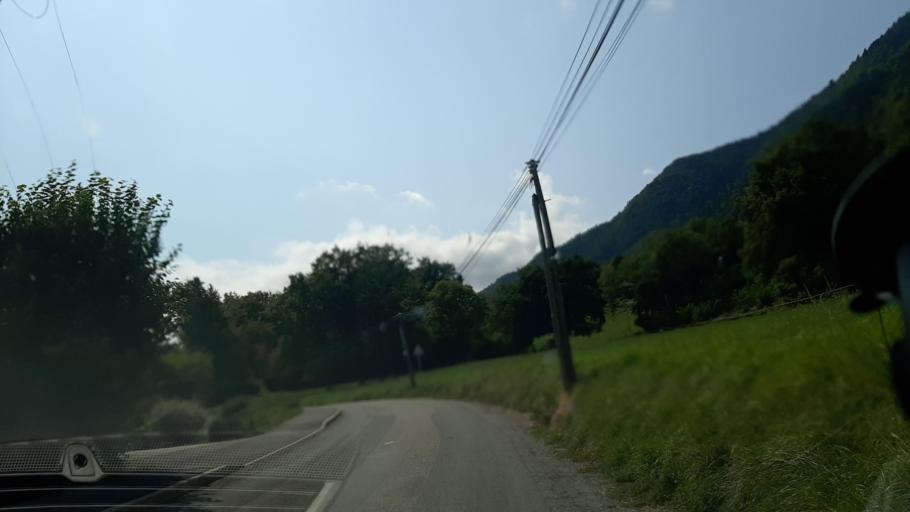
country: FR
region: Rhone-Alpes
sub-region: Departement de la Savoie
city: Mercury
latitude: 45.6815
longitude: 6.3461
